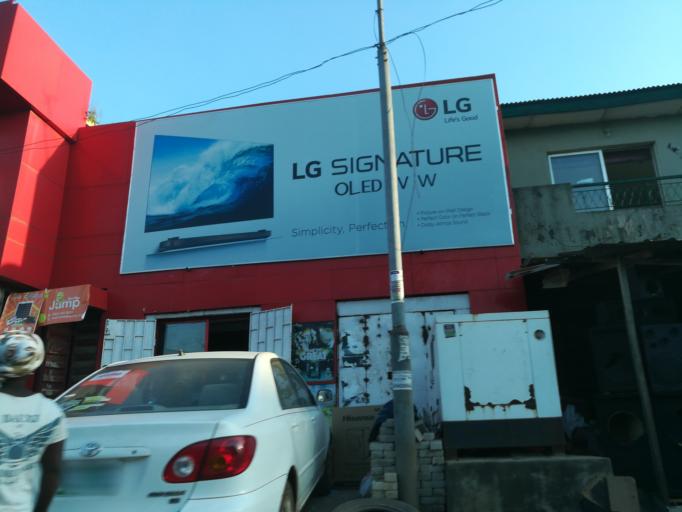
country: NG
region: Lagos
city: Ikorodu
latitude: 6.6186
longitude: 3.5053
